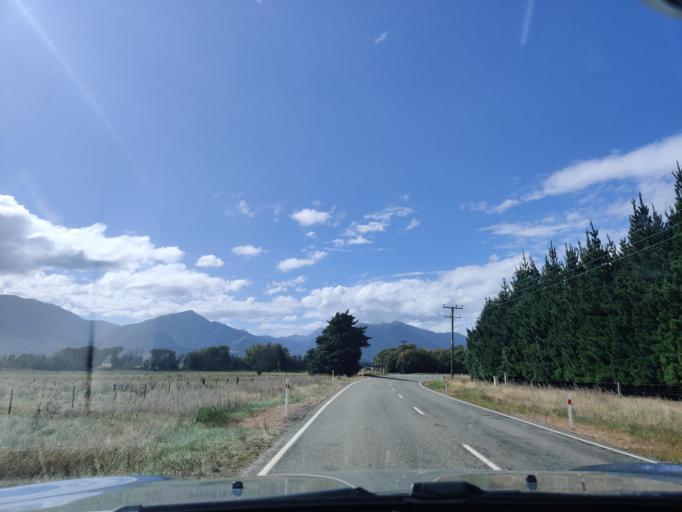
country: NZ
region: Canterbury
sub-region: Hurunui District
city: Amberley
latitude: -42.5651
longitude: 172.7937
